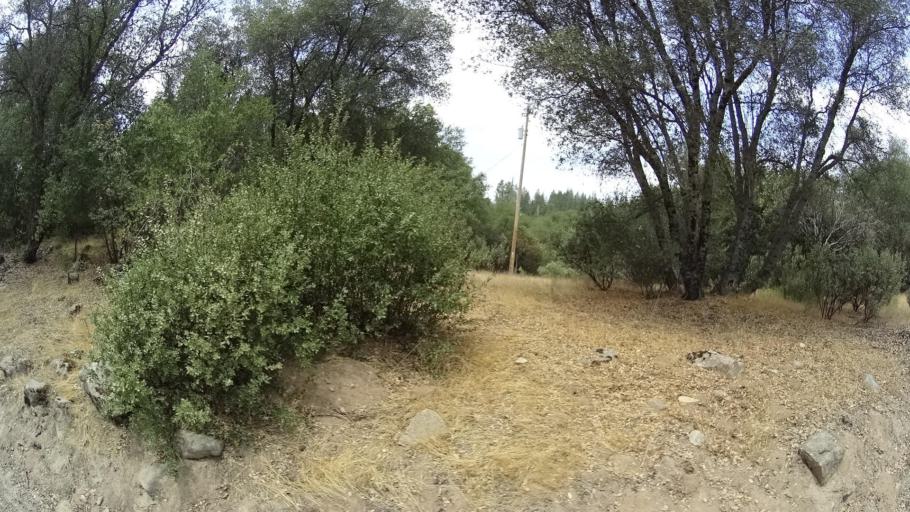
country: US
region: California
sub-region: Madera County
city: Ahwahnee
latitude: 37.4416
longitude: -119.8201
